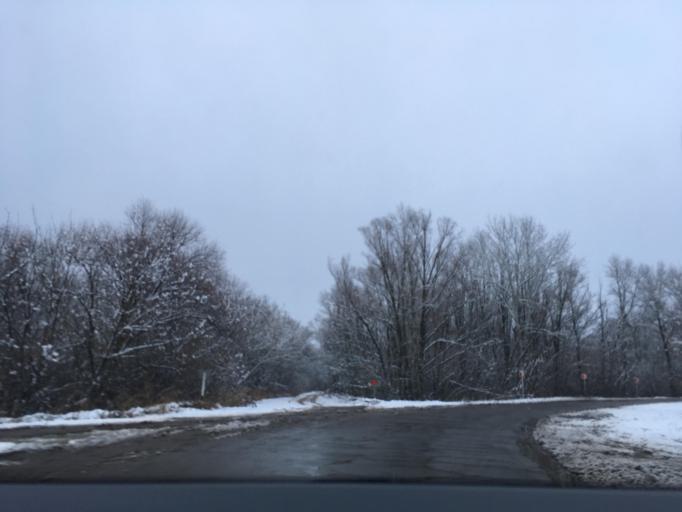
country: RU
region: Voronezj
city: Mitrofanovka
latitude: 50.1342
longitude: 39.9919
